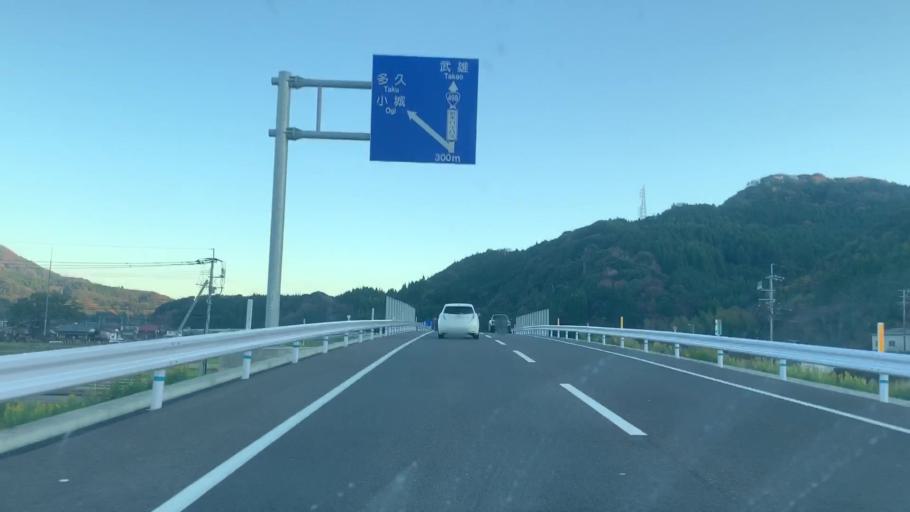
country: JP
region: Saga Prefecture
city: Takeocho-takeo
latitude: 33.2528
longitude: 129.9896
